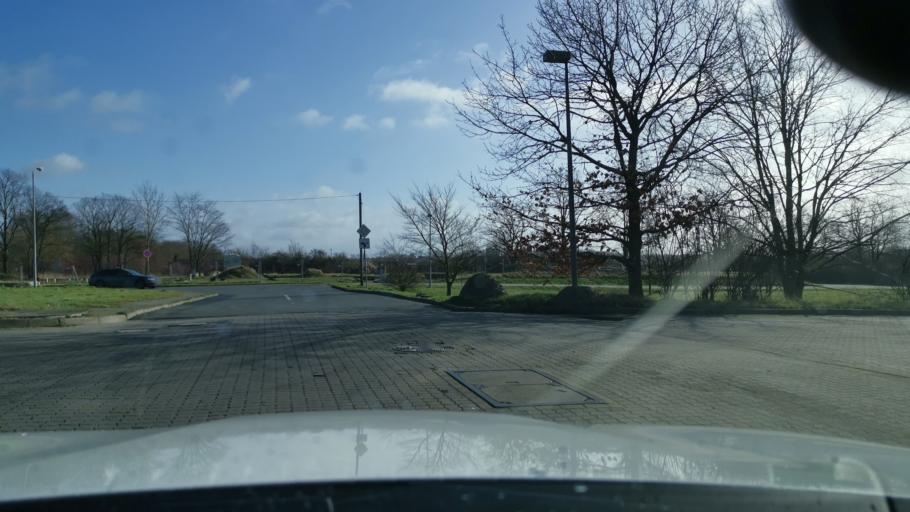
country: DE
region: Mecklenburg-Vorpommern
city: Lambrechtshagen
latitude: 54.1059
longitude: 12.0481
